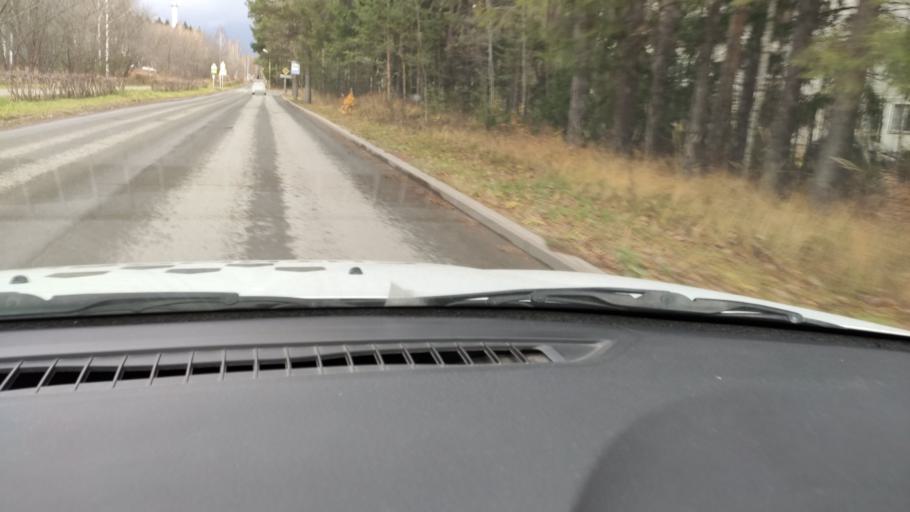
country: RU
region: Perm
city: Perm
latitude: 58.0507
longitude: 56.2137
